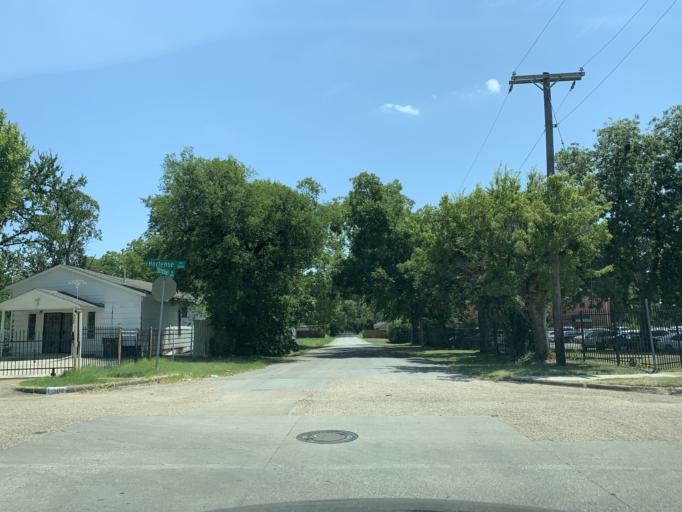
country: US
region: Texas
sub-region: Dallas County
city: Dallas
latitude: 32.6895
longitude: -96.8024
